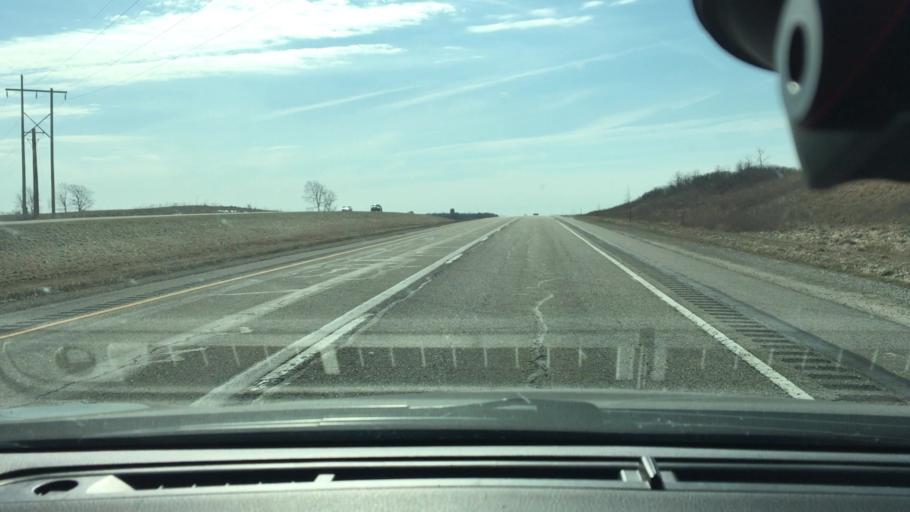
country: US
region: Iowa
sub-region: Floyd County
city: Charles City
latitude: 43.0017
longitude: -92.6121
